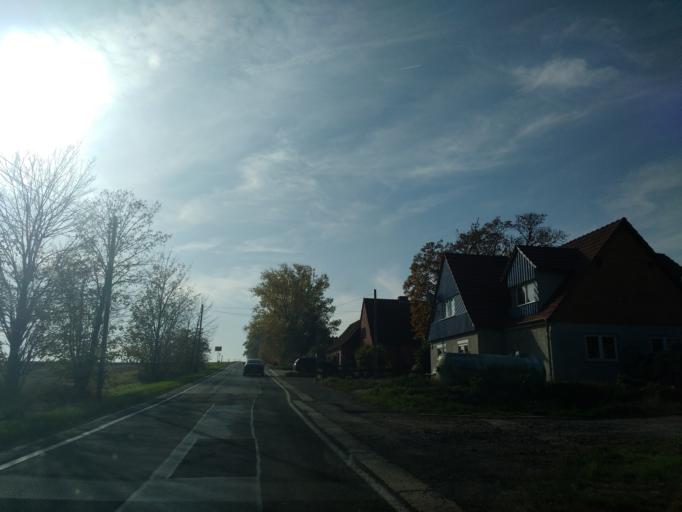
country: DE
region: Thuringia
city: Seebach
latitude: 51.1618
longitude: 10.5165
